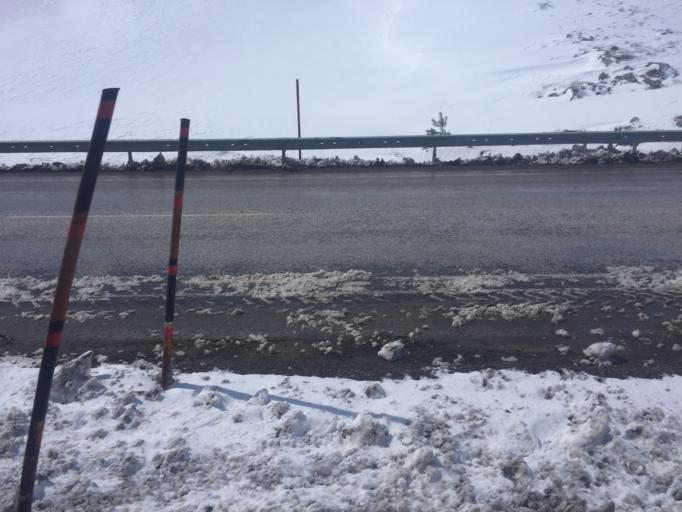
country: TR
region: Kahramanmaras
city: Goksun
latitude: 38.1983
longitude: 36.4553
